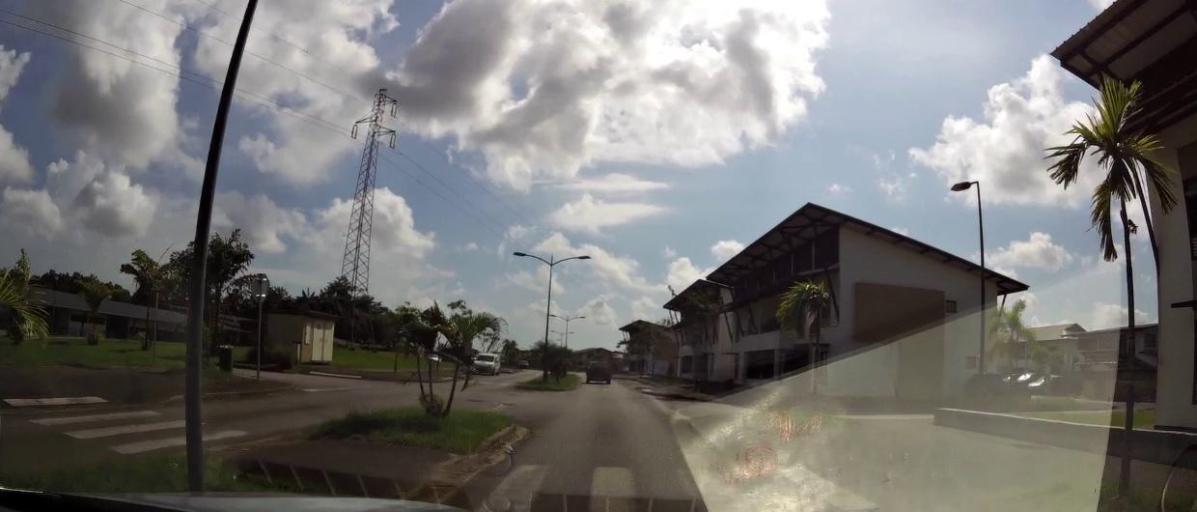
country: GF
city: Macouria
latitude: 4.9241
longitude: -52.4161
